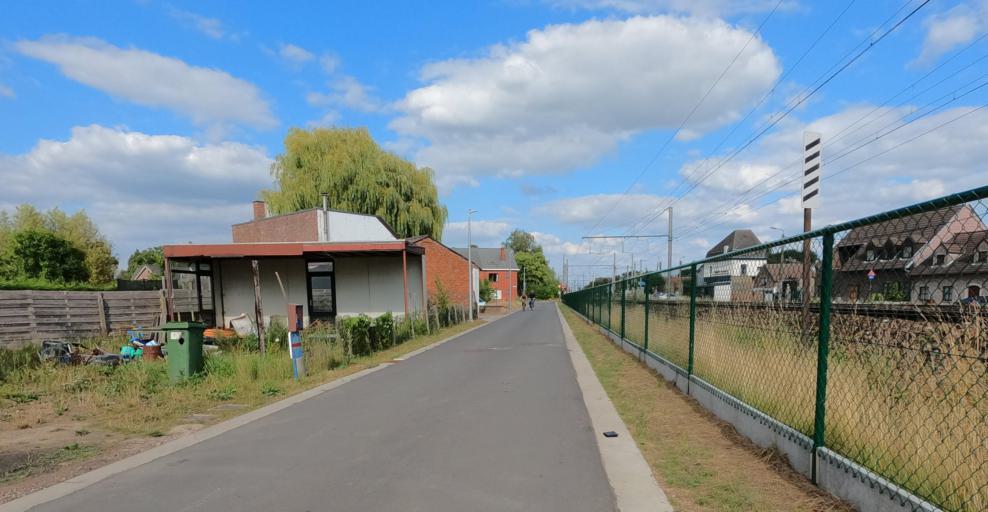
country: BE
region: Flanders
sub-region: Provincie Oost-Vlaanderen
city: Dendermonde
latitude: 51.0201
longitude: 4.0833
